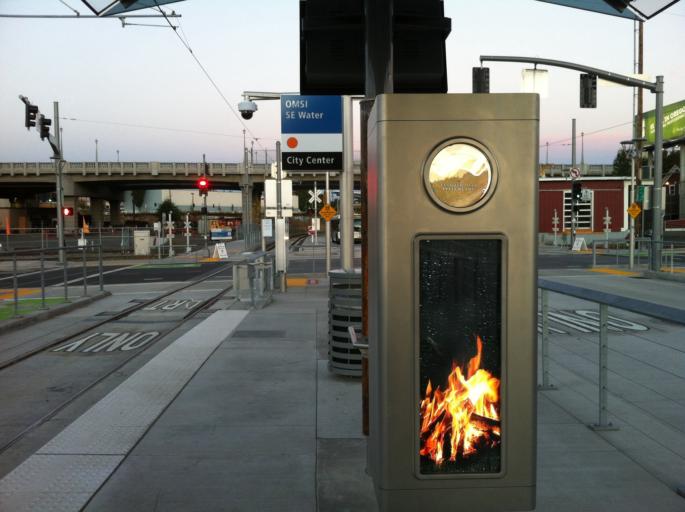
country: US
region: Oregon
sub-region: Multnomah County
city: Portland
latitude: 45.5066
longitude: -122.6624
